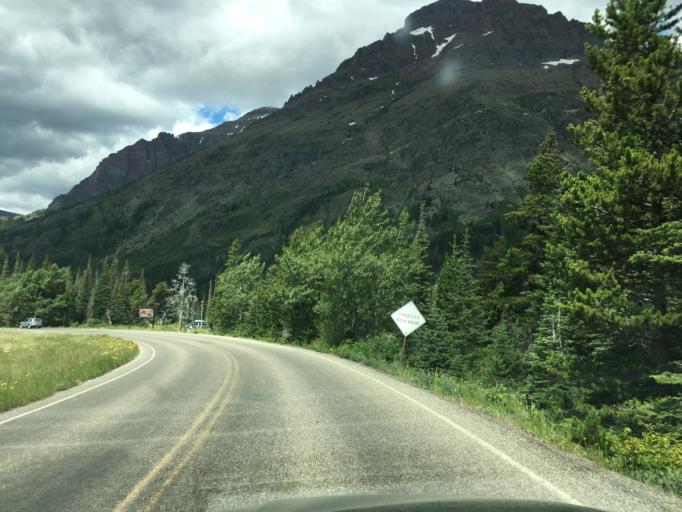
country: US
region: Montana
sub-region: Glacier County
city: South Browning
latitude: 48.4859
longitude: -113.3655
